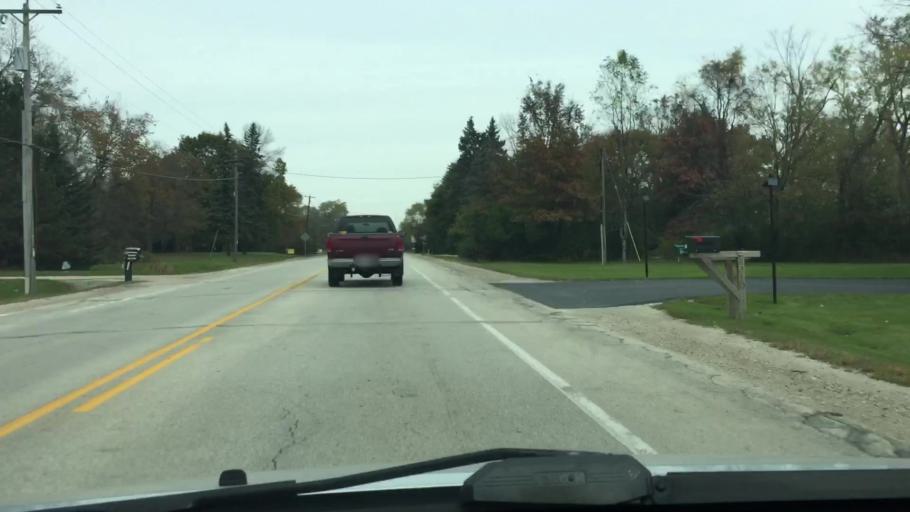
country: US
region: Wisconsin
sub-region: Milwaukee County
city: Franklin
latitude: 42.8938
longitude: -88.0394
